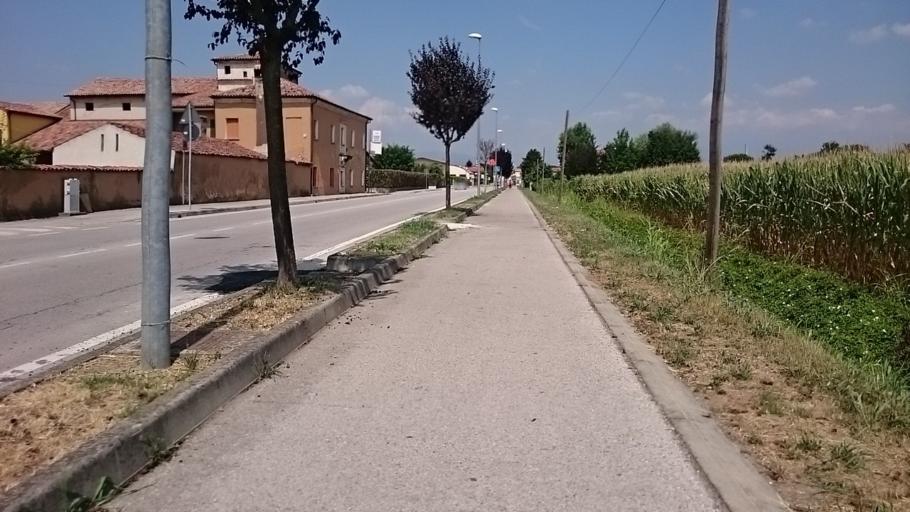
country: IT
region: Veneto
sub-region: Provincia di Padova
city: Cittadella
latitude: 45.6343
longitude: 11.7896
